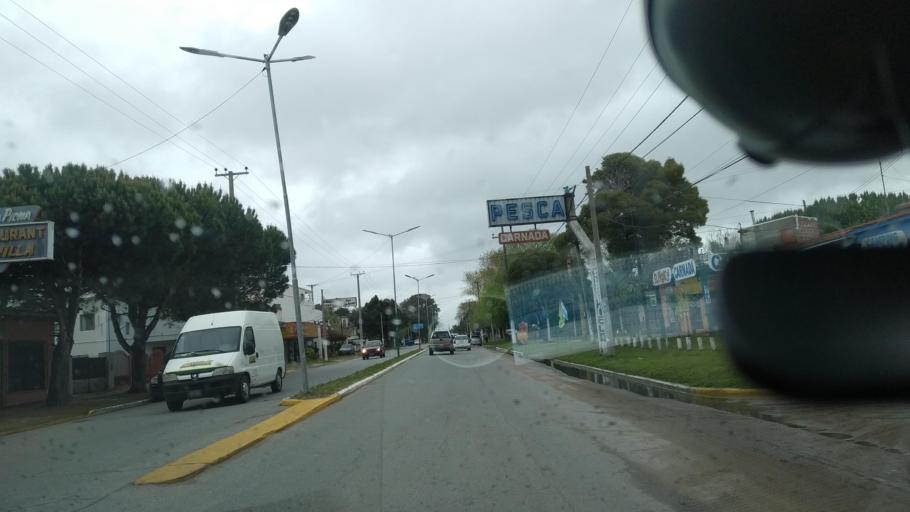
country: AR
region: Buenos Aires
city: San Clemente del Tuyu
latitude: -36.3743
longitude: -56.7185
